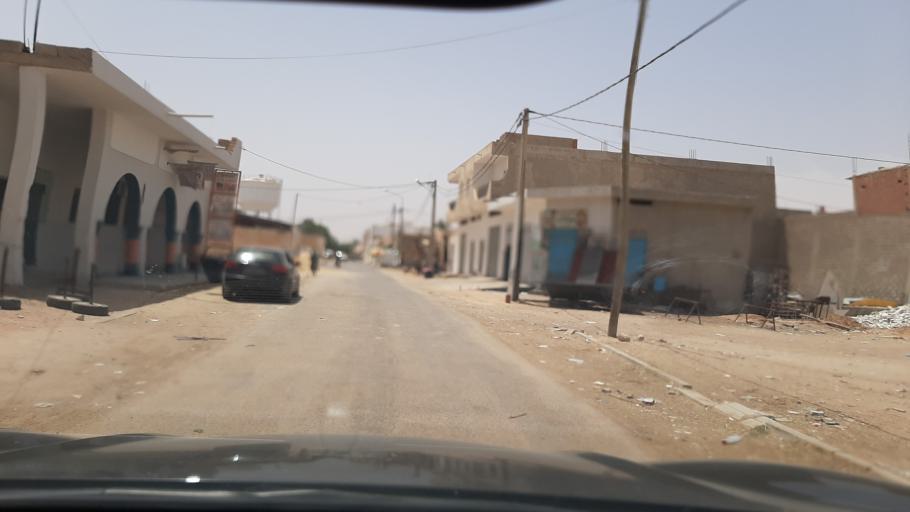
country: TN
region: Qabis
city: Gabes
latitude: 33.6197
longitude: 10.2898
